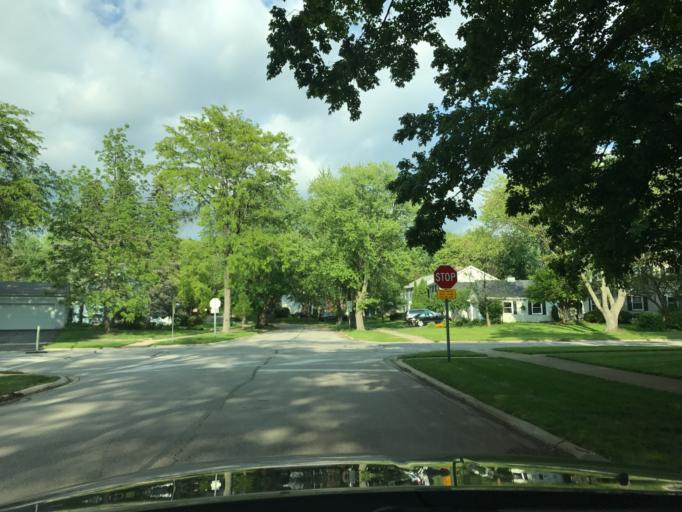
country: US
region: Illinois
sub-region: DuPage County
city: Naperville
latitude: 41.7880
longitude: -88.1417
